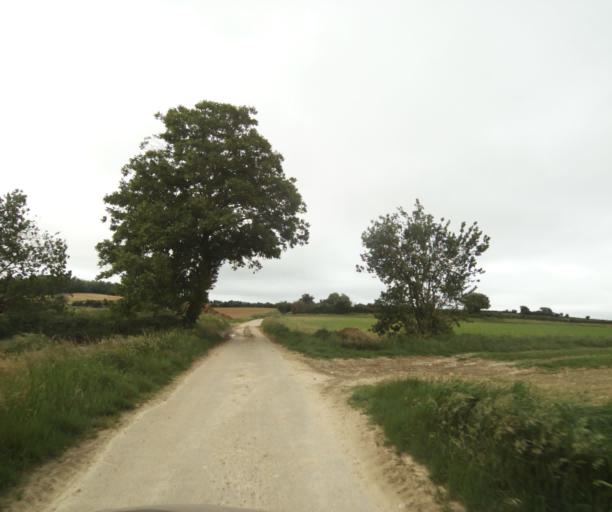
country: FR
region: Rhone-Alpes
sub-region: Departement de l'Ain
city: Miribel
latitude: 45.8421
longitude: 4.9440
